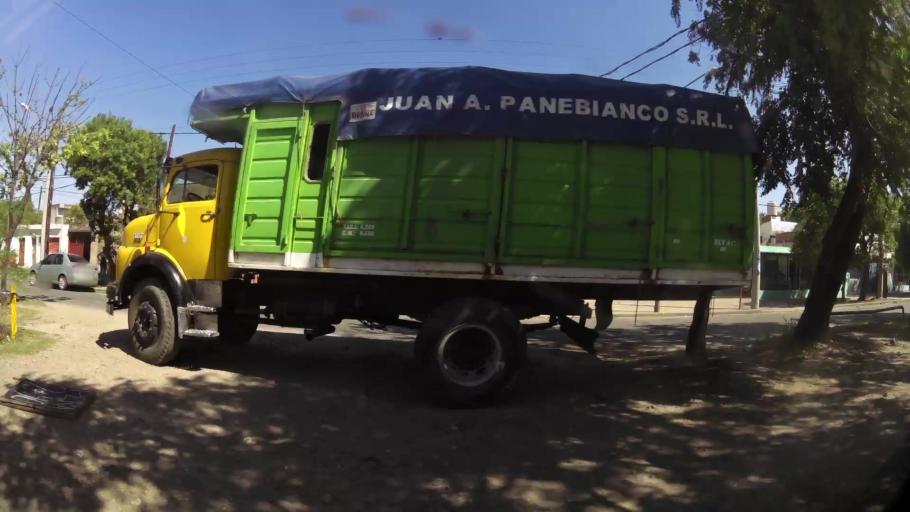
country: AR
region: Cordoba
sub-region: Departamento de Capital
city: Cordoba
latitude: -31.3677
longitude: -64.1728
